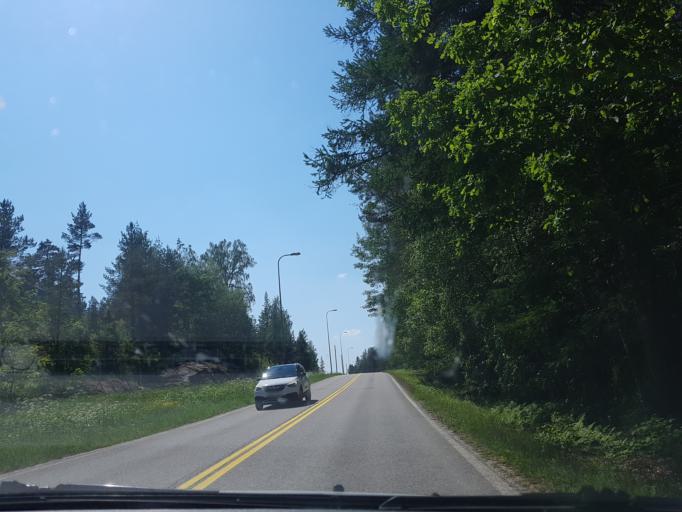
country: FI
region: Uusimaa
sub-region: Helsinki
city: Vihti
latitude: 60.3337
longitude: 24.4302
